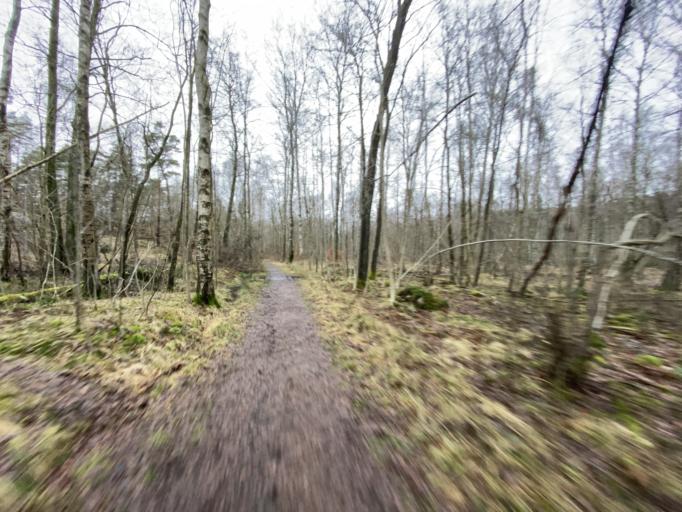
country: SE
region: Vaestra Goetaland
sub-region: Molndal
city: Moelndal
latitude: 57.7058
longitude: 12.0347
